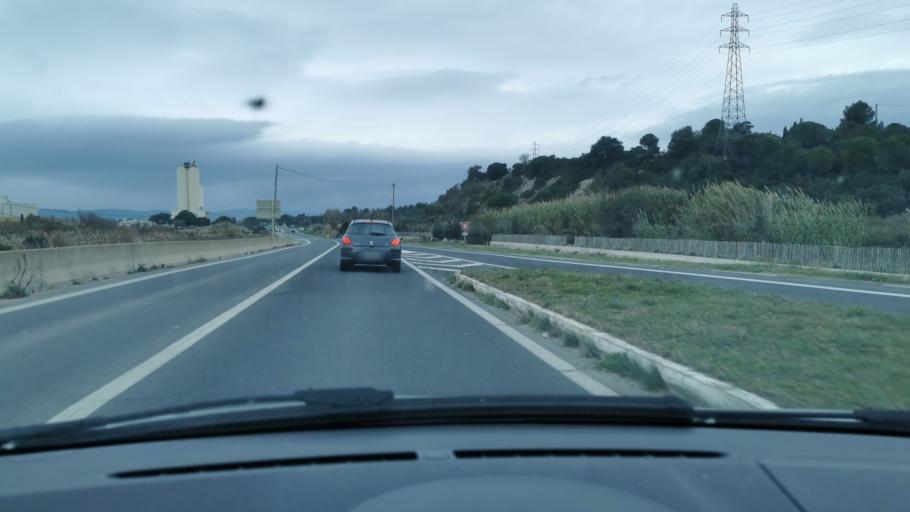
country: FR
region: Languedoc-Roussillon
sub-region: Departement de l'Herault
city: Sete
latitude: 43.4250
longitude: 3.7078
